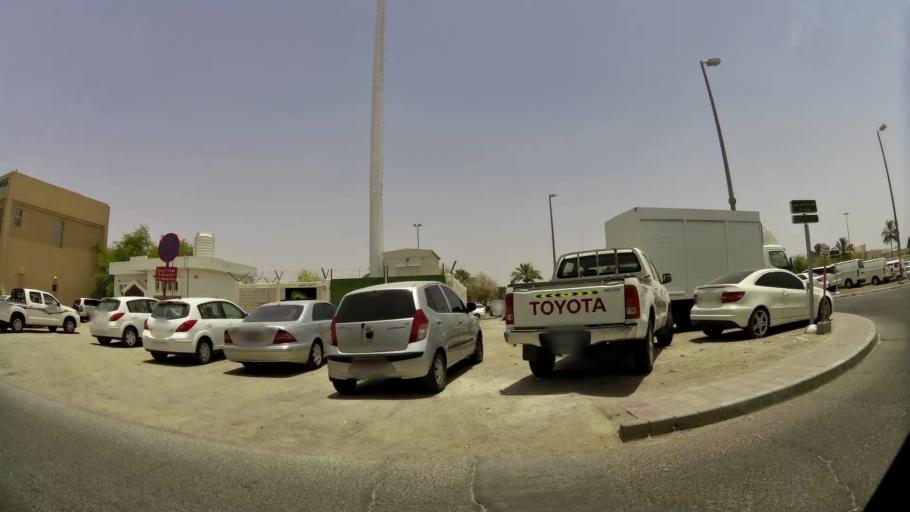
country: AE
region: Abu Dhabi
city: Al Ain
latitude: 24.2125
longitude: 55.7542
